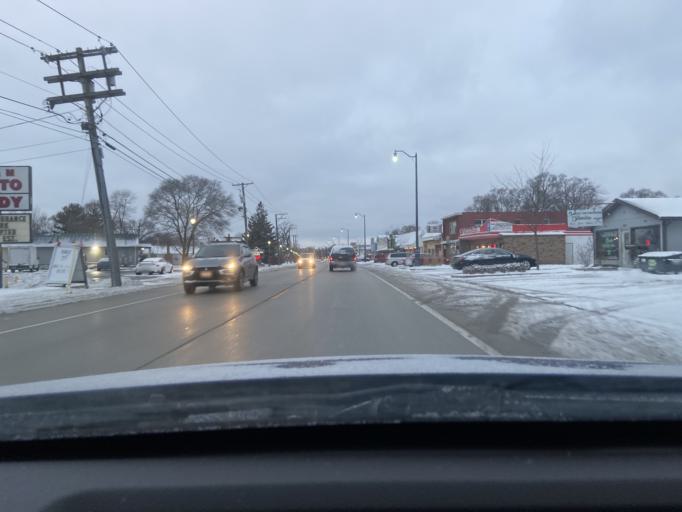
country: US
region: Illinois
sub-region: Lake County
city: Round Lake Park
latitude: 42.3484
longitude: -88.0775
